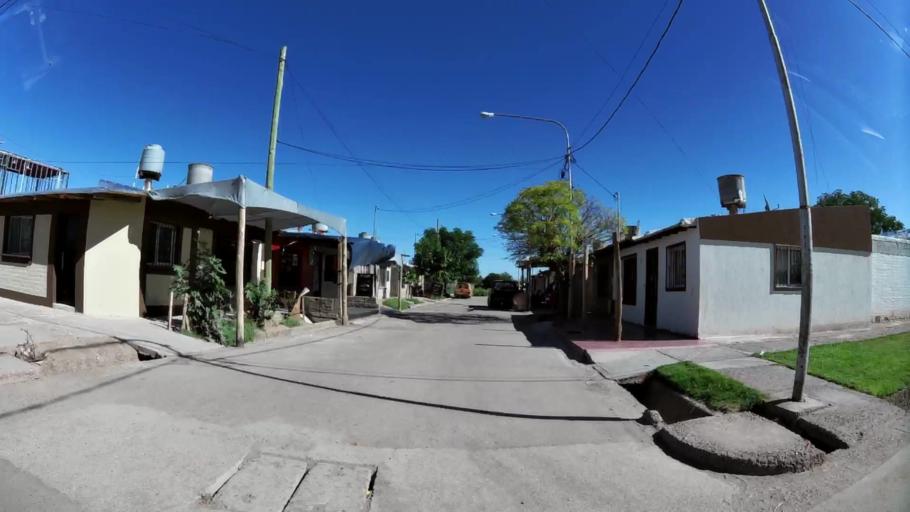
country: AR
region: Mendoza
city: Las Heras
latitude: -32.8388
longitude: -68.8116
